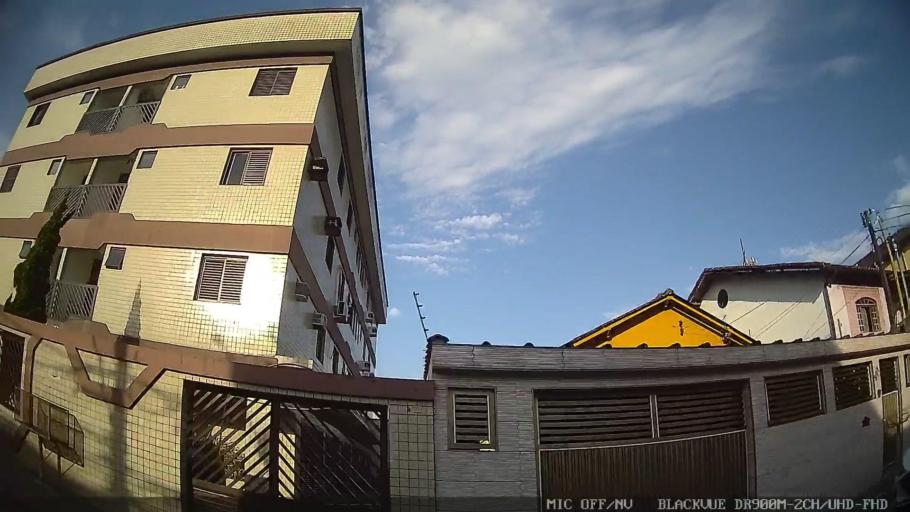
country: BR
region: Sao Paulo
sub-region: Cubatao
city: Cubatao
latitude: -23.8996
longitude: -46.4252
